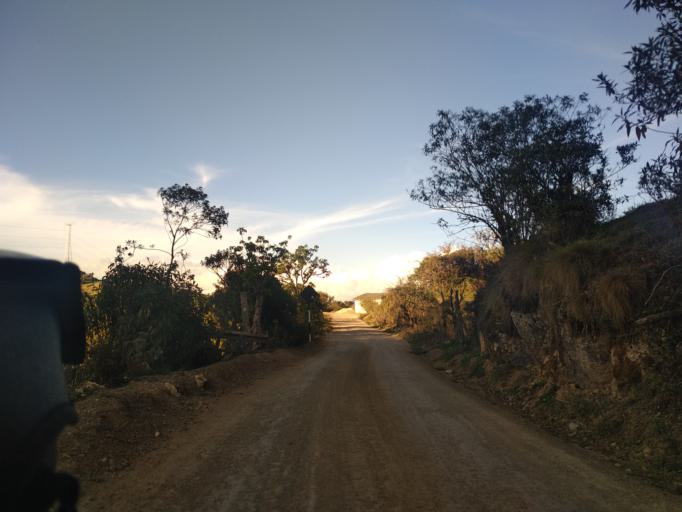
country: PE
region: Amazonas
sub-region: Provincia de Chachapoyas
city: Montevideo
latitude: -6.7182
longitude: -77.8663
